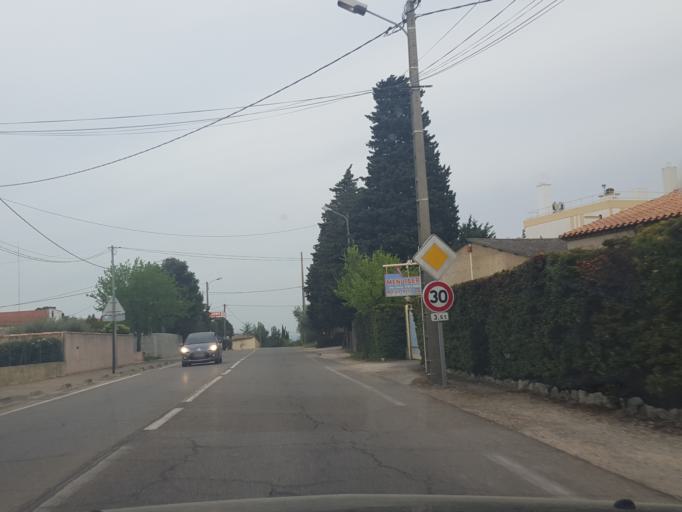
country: FR
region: Provence-Alpes-Cote d'Azur
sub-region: Departement du Vaucluse
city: Chateauneuf-de-Gadagne
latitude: 43.9291
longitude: 4.9363
